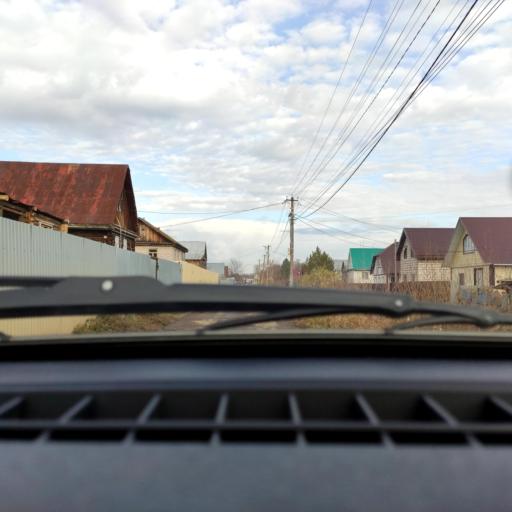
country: RU
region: Bashkortostan
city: Ufa
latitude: 54.6315
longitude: 55.8900
